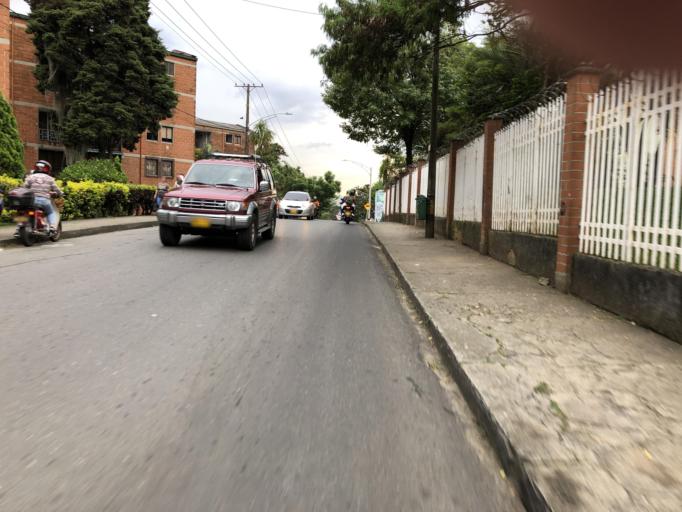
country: CO
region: Antioquia
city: Medellin
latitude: 6.2930
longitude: -75.5668
